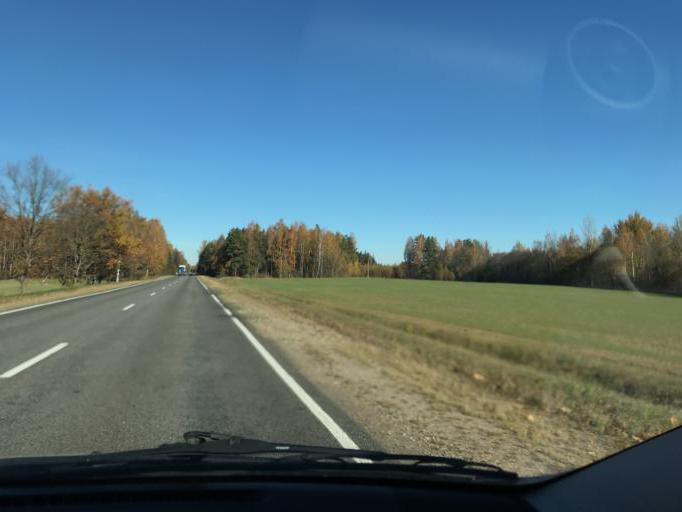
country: BY
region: Vitebsk
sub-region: Ushatski Rayon
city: Ushachy
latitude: 55.0896
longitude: 28.7565
